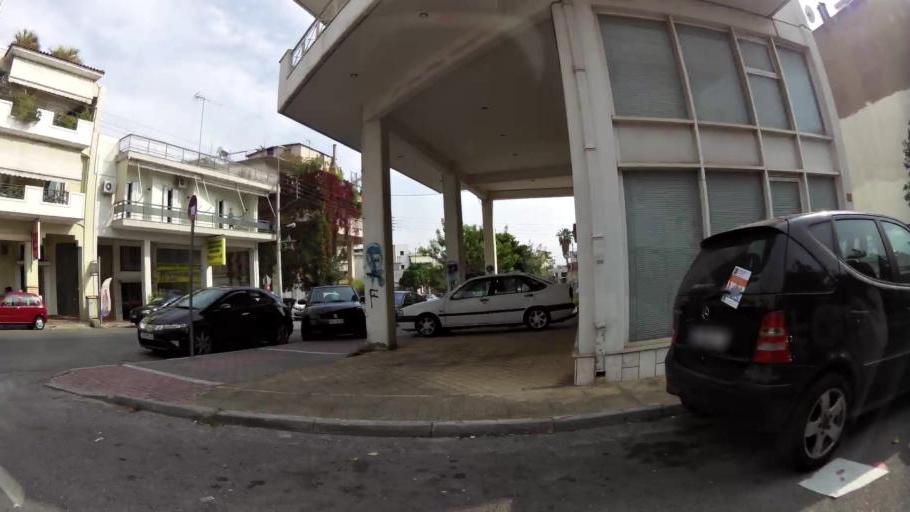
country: GR
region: Attica
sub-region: Nomarchia Athinas
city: Chaidari
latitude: 38.0132
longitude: 23.6751
